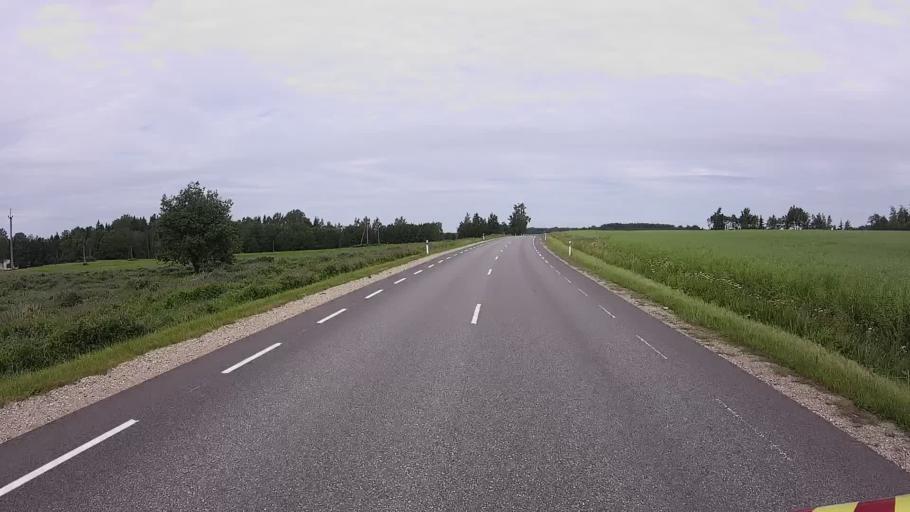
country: EE
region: Viljandimaa
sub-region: Karksi vald
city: Karksi-Nuia
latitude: 58.1613
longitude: 25.5887
